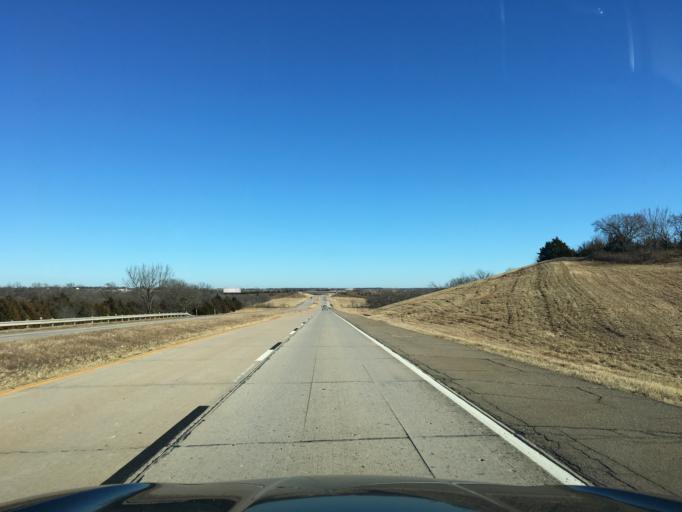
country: US
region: Oklahoma
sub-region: Payne County
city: Yale
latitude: 36.2243
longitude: -96.7219
